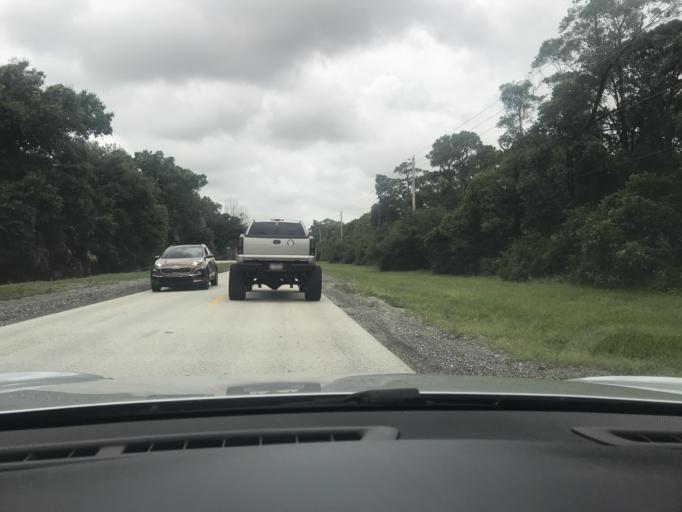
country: US
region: Florida
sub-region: Indian River County
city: Vero Beach South
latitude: 27.6461
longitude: -80.4426
